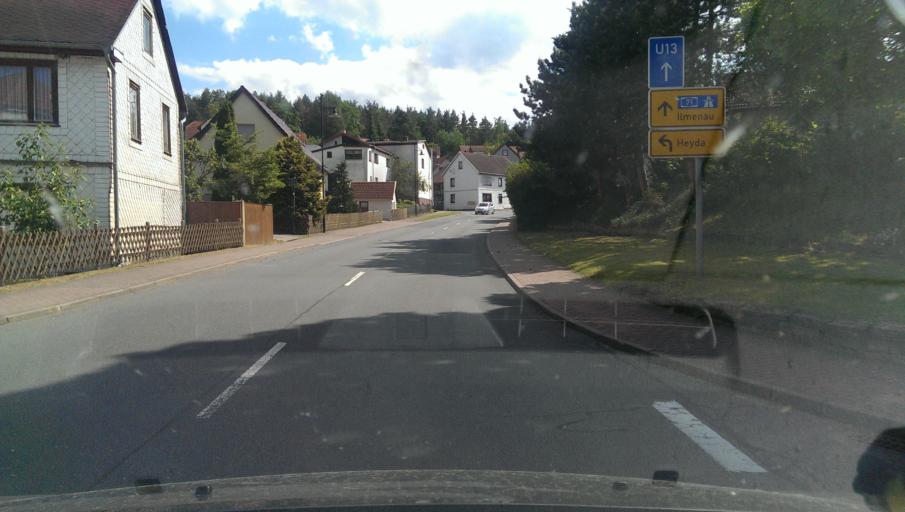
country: DE
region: Thuringia
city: Martinroda
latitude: 50.7238
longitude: 10.8880
